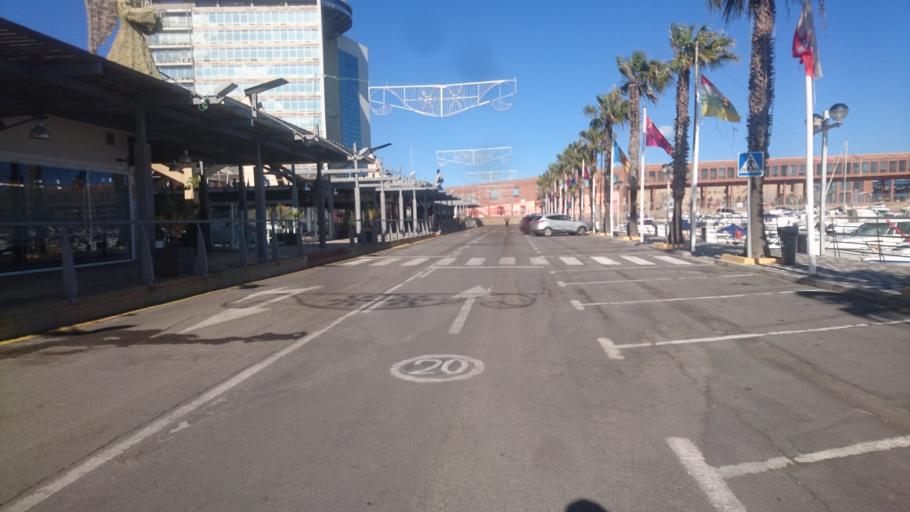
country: ES
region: Melilla
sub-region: Melilla
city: Melilla
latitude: 35.2884
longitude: -2.9355
